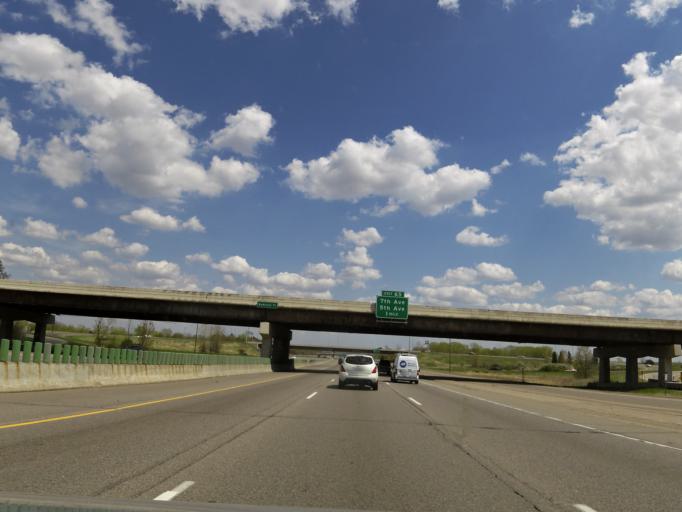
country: US
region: Minnesota
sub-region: Dakota County
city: Inver Grove Heights
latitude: 44.8747
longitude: -93.0655
